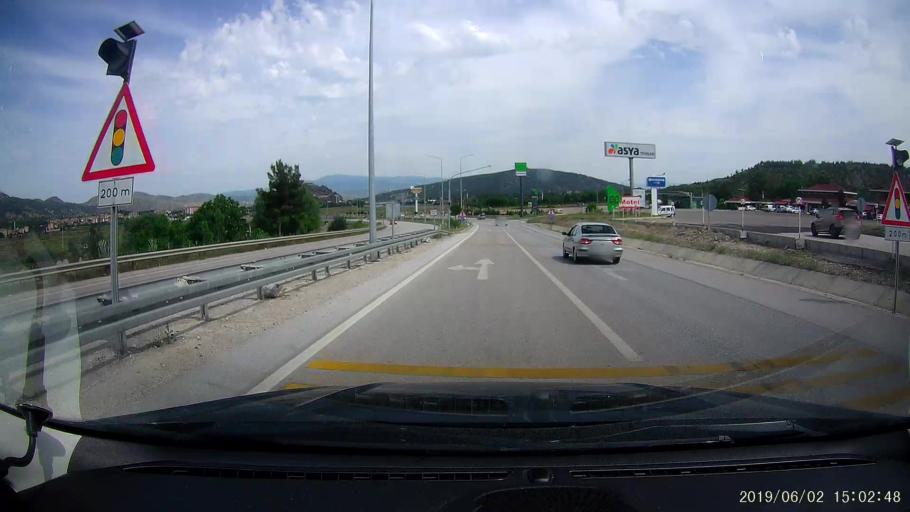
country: TR
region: Corum
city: Osmancik
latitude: 40.9784
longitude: 34.7717
